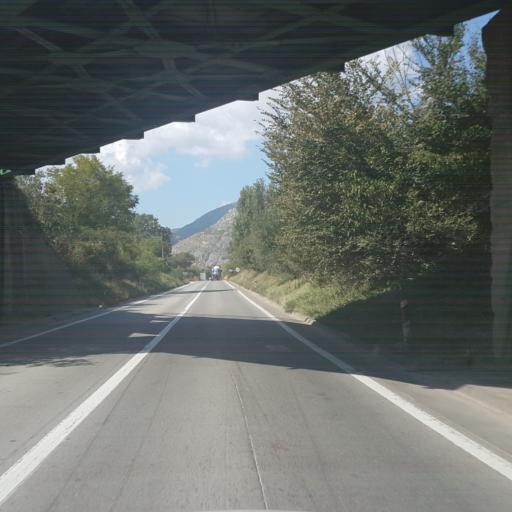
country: RS
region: Central Serbia
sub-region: Pirotski Okrug
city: Bela Palanka
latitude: 43.2987
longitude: 22.1994
